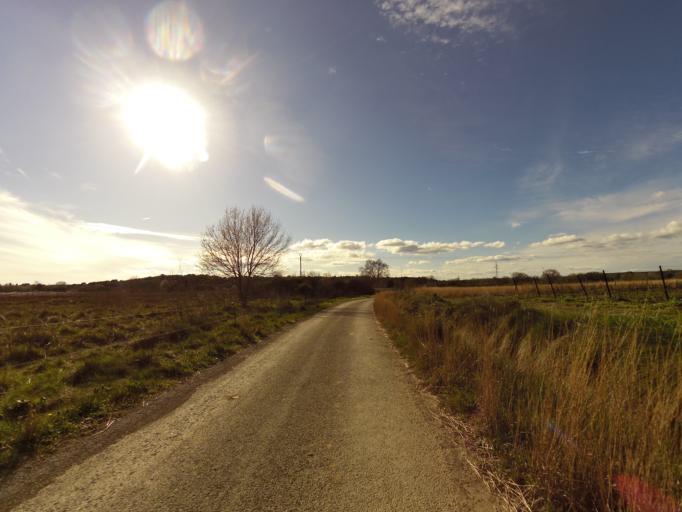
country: FR
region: Languedoc-Roussillon
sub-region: Departement du Gard
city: Gallargues-le-Montueux
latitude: 43.7185
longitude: 4.1612
